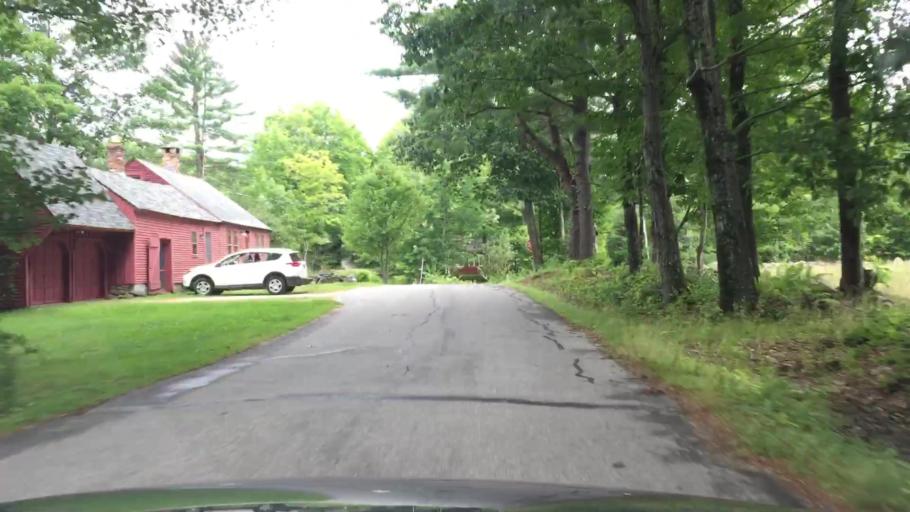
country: US
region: New Hampshire
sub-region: Carroll County
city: Sandwich
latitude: 43.8020
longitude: -71.4725
